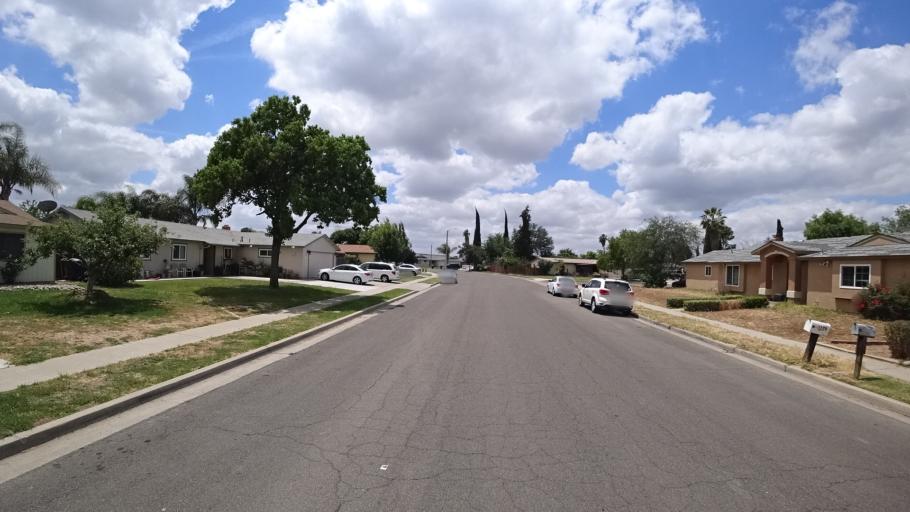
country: US
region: California
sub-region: Kings County
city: Hanford
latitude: 36.3108
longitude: -119.6696
